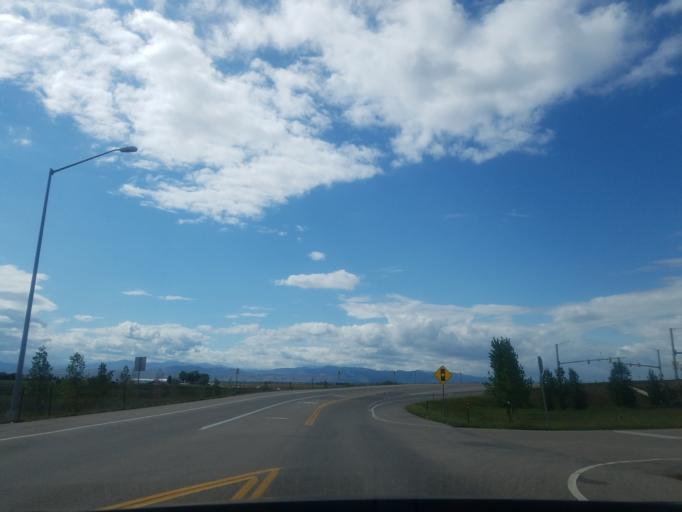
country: US
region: Colorado
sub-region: Weld County
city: Windsor
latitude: 40.4782
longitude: -104.9934
